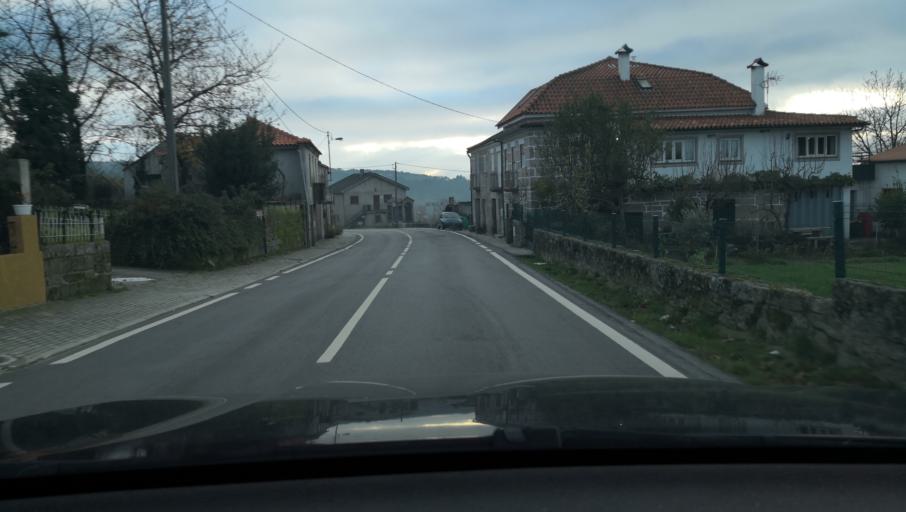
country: PT
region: Vila Real
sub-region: Vila Real
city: Vila Real
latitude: 41.3361
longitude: -7.6639
